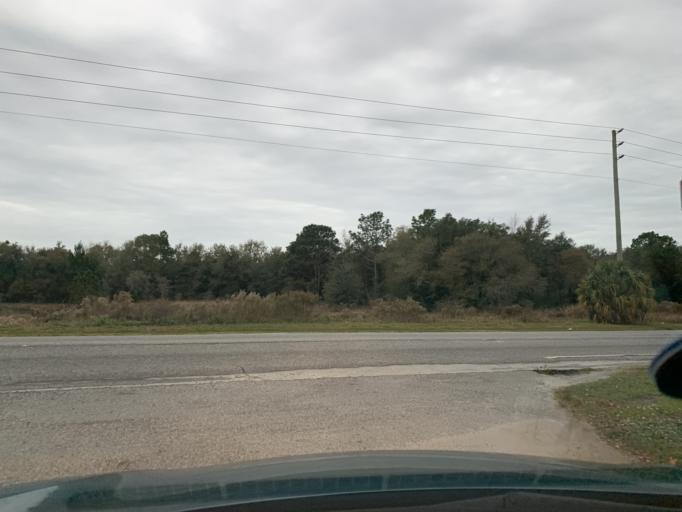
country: US
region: Florida
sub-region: Hernando County
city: Timber Pines
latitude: 28.4341
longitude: -82.5901
